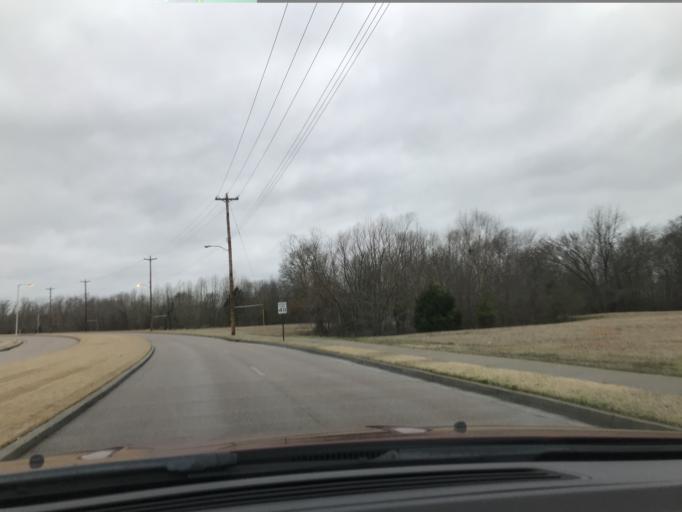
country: US
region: Tennessee
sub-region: Shelby County
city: Collierville
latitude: 35.0819
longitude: -89.6823
